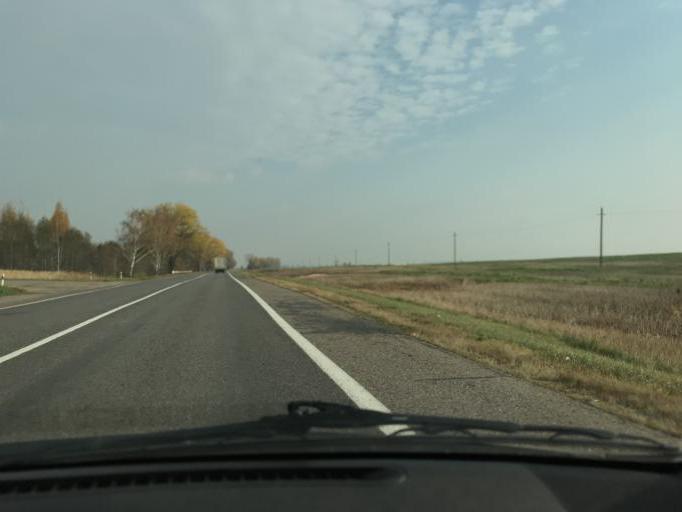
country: BY
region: Vitebsk
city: Chashniki
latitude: 55.0079
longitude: 28.9781
